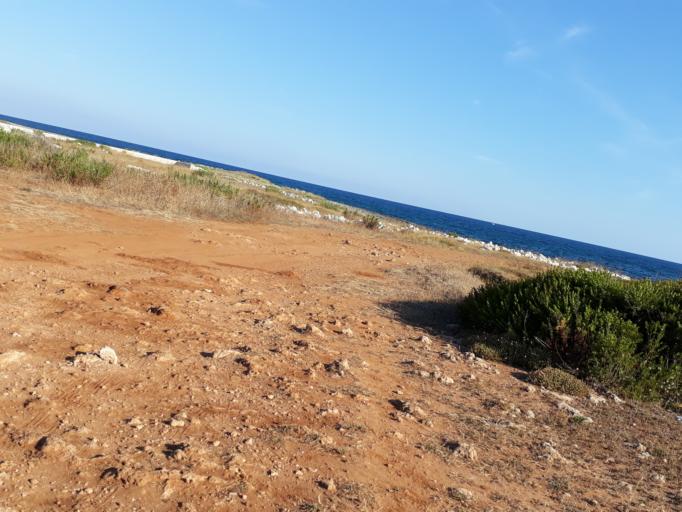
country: IT
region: Apulia
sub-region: Provincia di Brindisi
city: Carovigno
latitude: 40.7641
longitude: 17.6877
